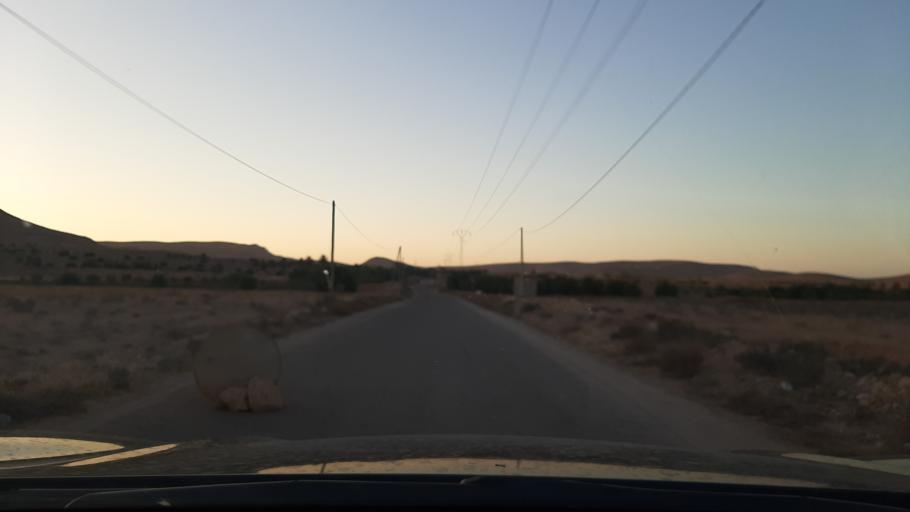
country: TN
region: Qabis
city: Matmata
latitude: 33.5508
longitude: 10.1882
